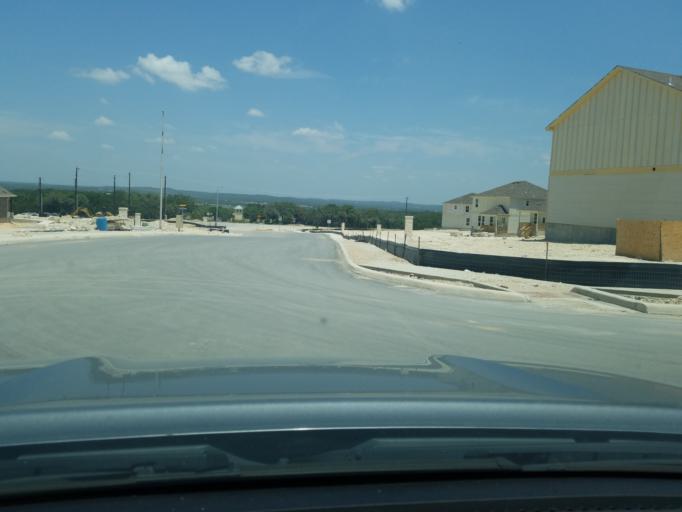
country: US
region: Texas
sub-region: Bexar County
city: Timberwood Park
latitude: 29.7067
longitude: -98.4996
